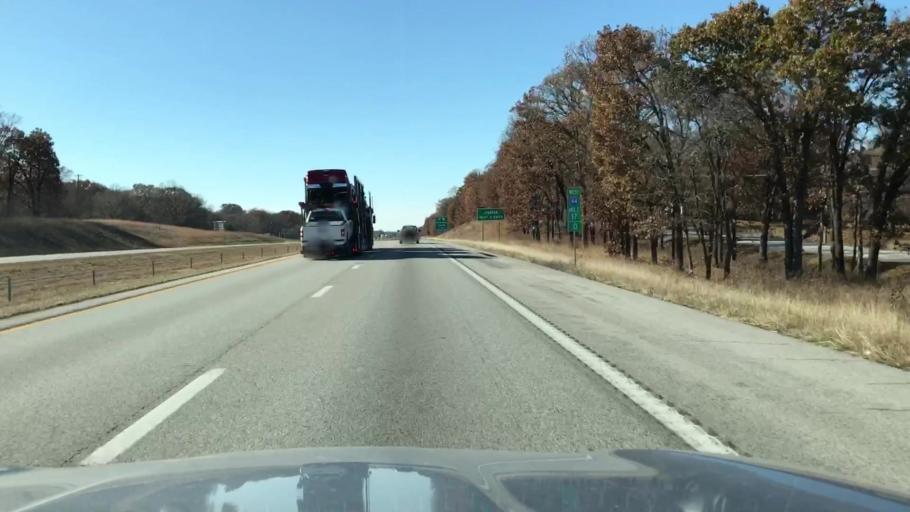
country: US
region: Missouri
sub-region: Jasper County
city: Duenweg
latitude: 37.0822
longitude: -94.3392
